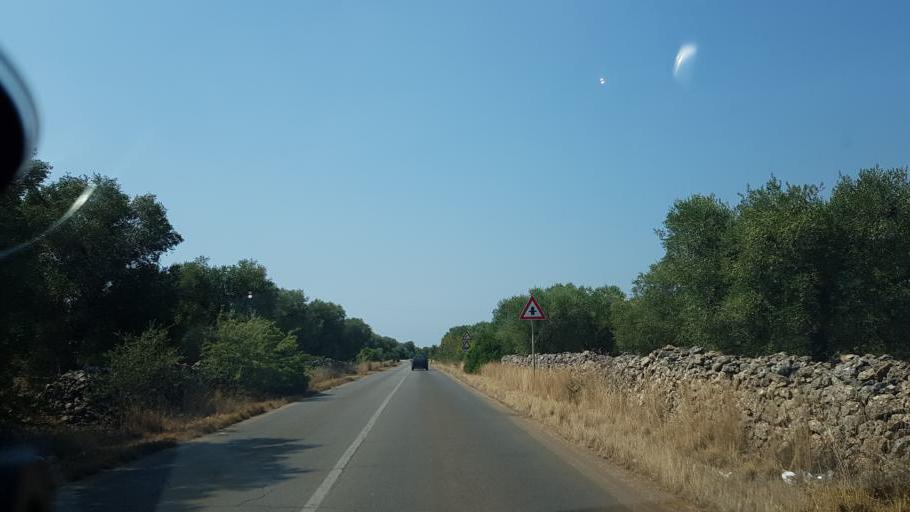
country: IT
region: Apulia
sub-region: Provincia di Taranto
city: Maruggio
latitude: 40.3423
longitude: 17.5906
